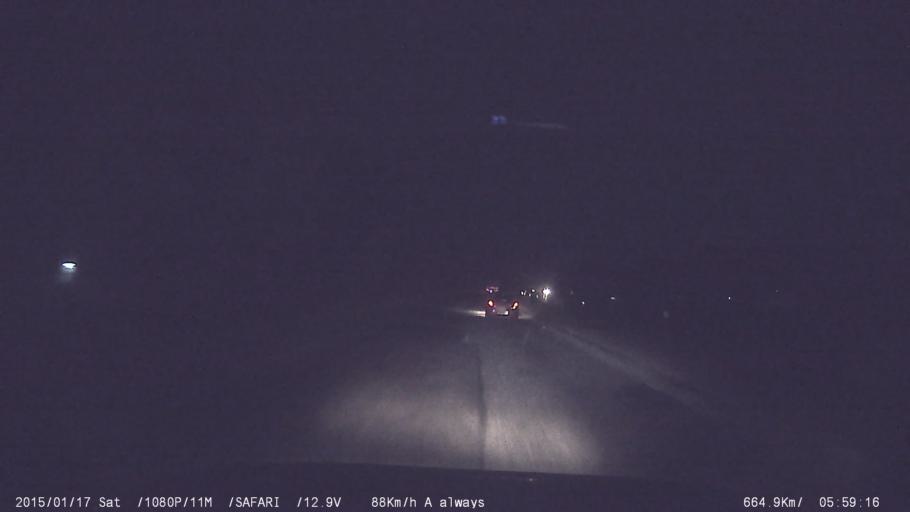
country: IN
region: Tamil Nadu
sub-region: Kancheepuram
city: Kanchipuram
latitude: 12.8979
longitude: 79.5634
